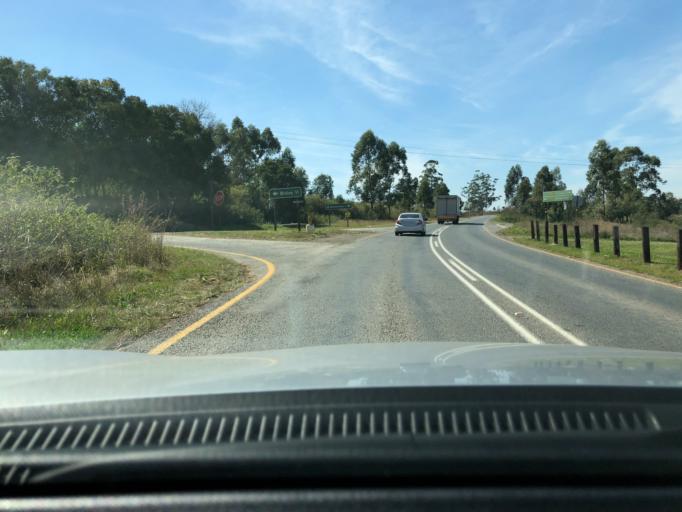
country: ZA
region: KwaZulu-Natal
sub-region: uMgungundlovu District Municipality
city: Camperdown
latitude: -29.7348
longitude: 30.4328
